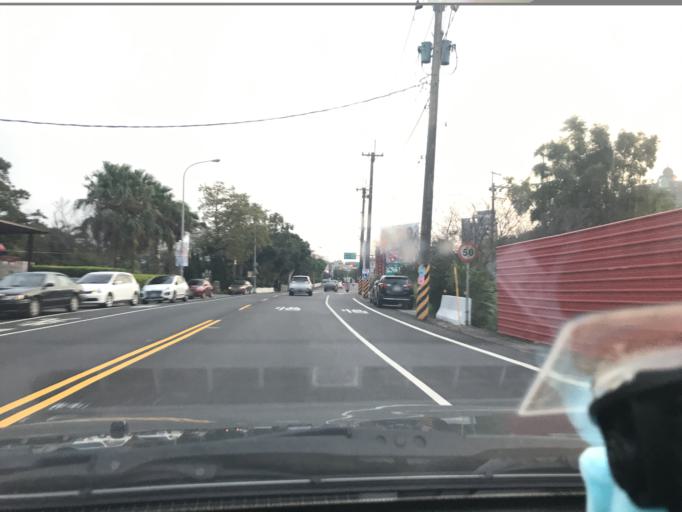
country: TW
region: Taiwan
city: Daxi
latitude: 24.8728
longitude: 121.2188
